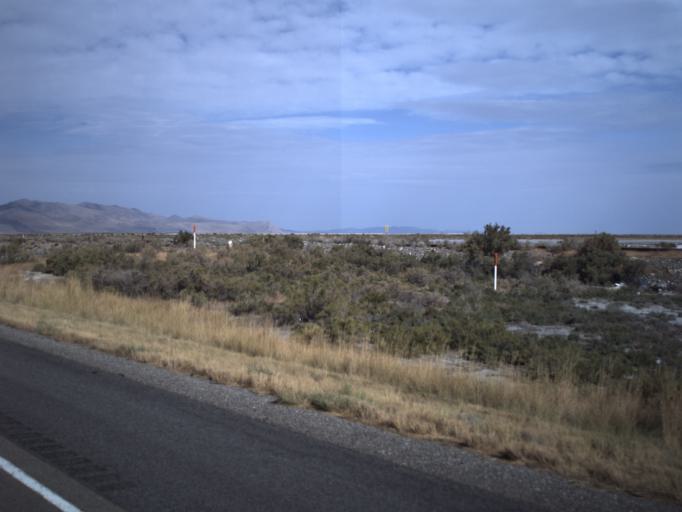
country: US
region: Utah
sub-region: Tooele County
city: Grantsville
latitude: 40.7406
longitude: -112.6235
